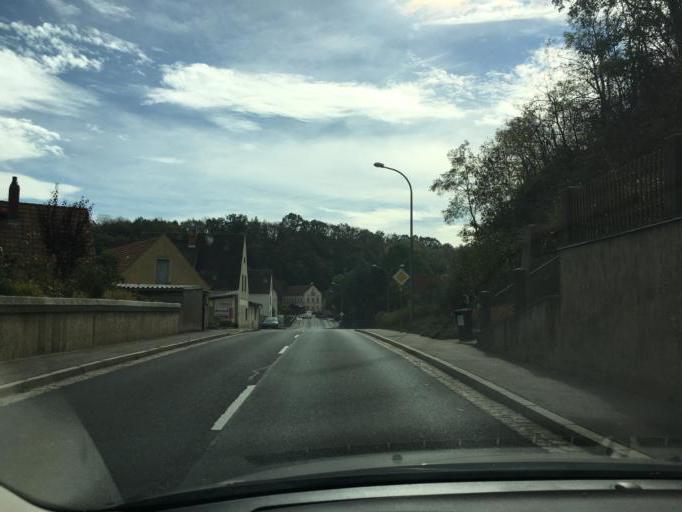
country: DE
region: Saxony
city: Meissen
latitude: 51.1989
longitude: 13.4054
